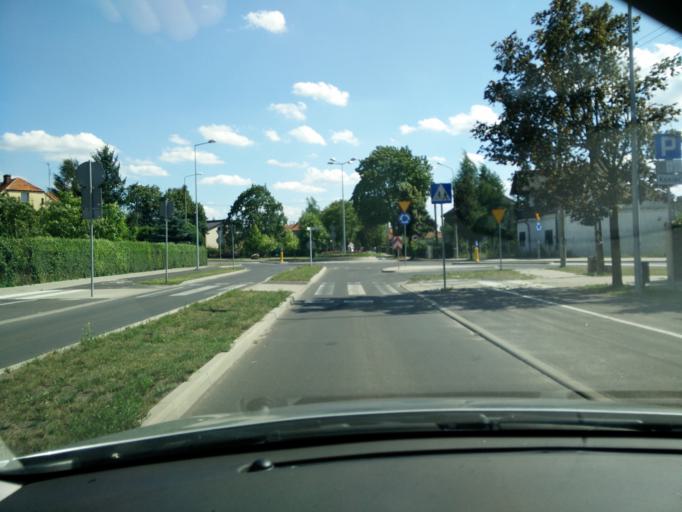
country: PL
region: Greater Poland Voivodeship
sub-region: Powiat sredzki
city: Sroda Wielkopolska
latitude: 52.2280
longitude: 17.2654
